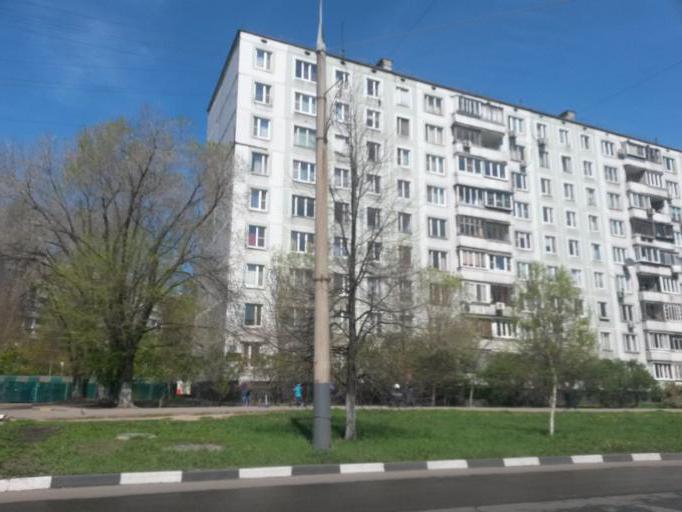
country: RU
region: Moscow
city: Mar'ino
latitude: 55.6469
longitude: 37.7161
